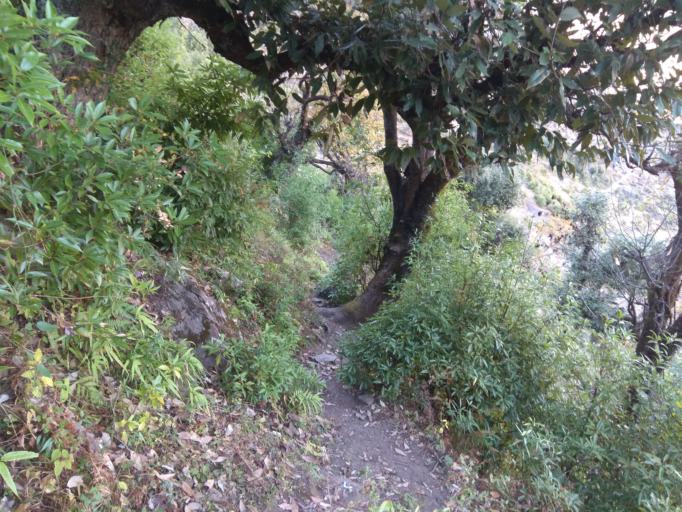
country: NP
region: Mid Western
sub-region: Karnali Zone
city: Jumla
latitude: 29.3153
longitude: 81.7235
